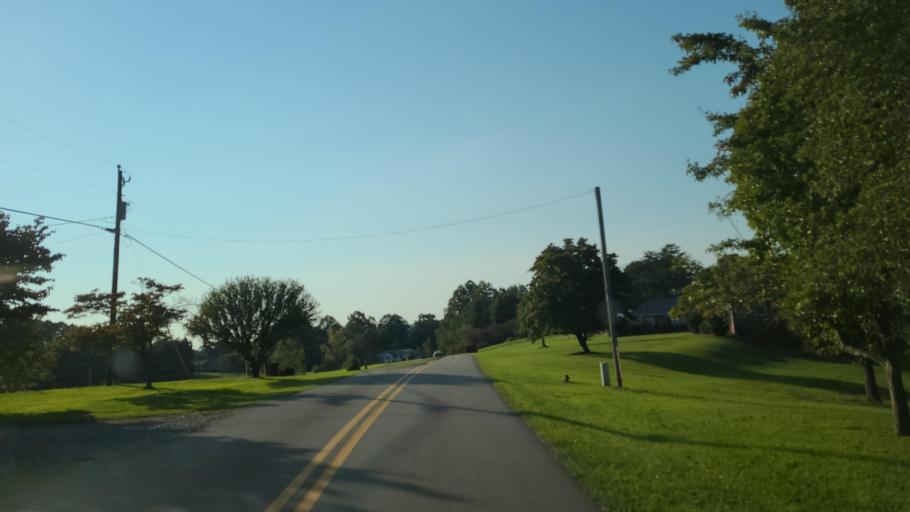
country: US
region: Georgia
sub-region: Pickens County
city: Jasper
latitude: 34.4009
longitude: -84.4558
